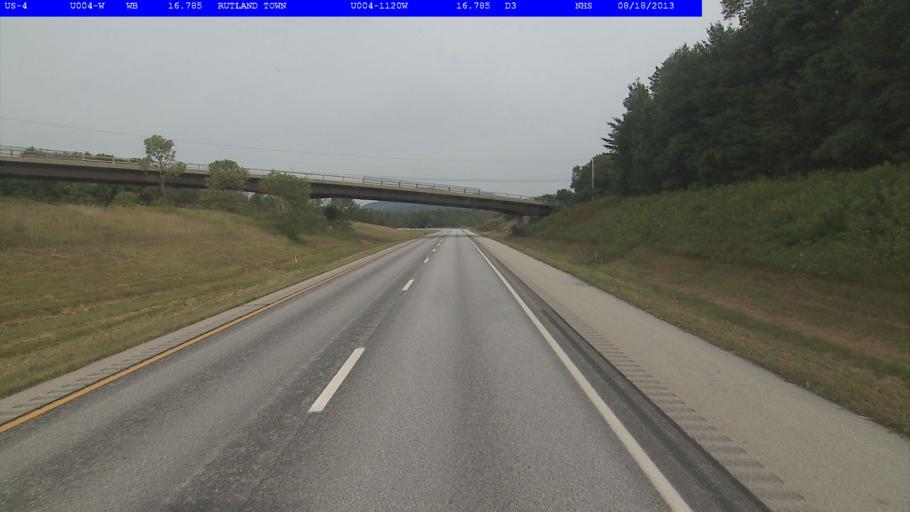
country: US
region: Vermont
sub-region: Rutland County
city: Rutland
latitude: 43.5907
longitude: -73.0031
